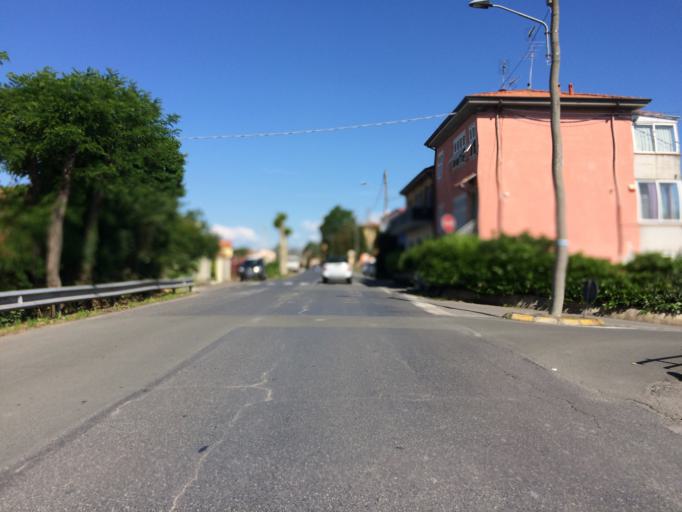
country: IT
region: Liguria
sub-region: Provincia di La Spezia
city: Sarzana
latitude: 44.1039
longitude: 9.9770
